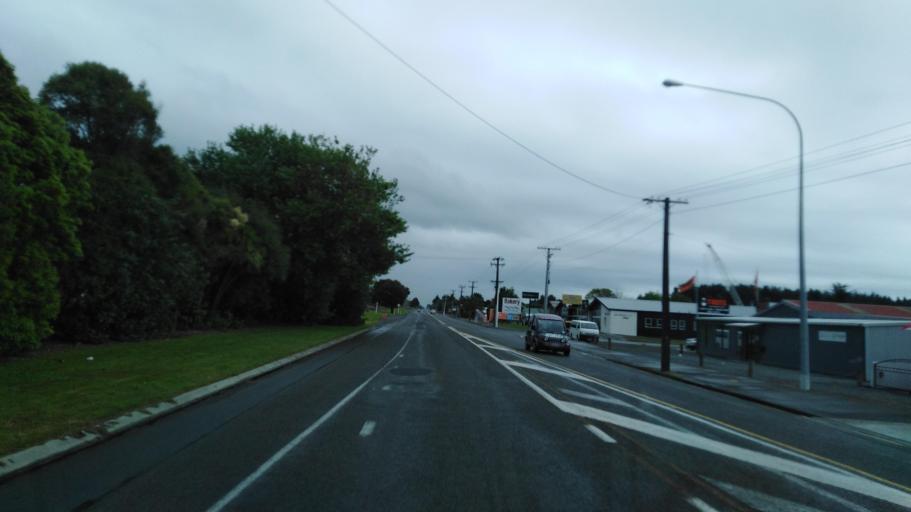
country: NZ
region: Manawatu-Wanganui
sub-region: Horowhenua District
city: Levin
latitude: -40.6367
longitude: 175.2721
